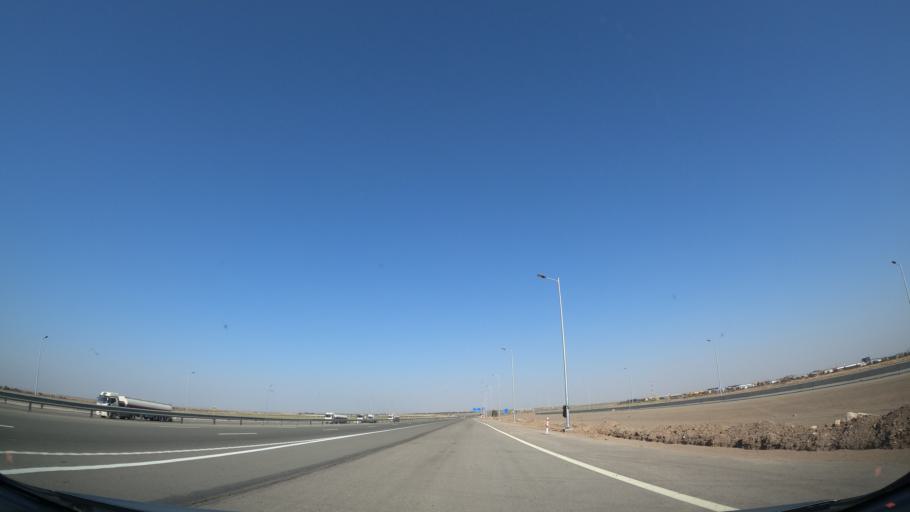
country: IR
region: Tehran
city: Eqbaliyeh
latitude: 35.1376
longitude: 51.5222
